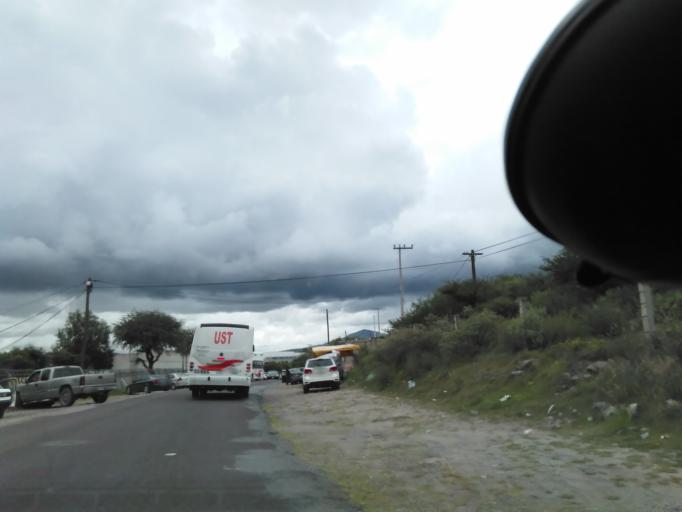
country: MX
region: Hidalgo
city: Tula de Allende
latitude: 20.0602
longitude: -99.3610
